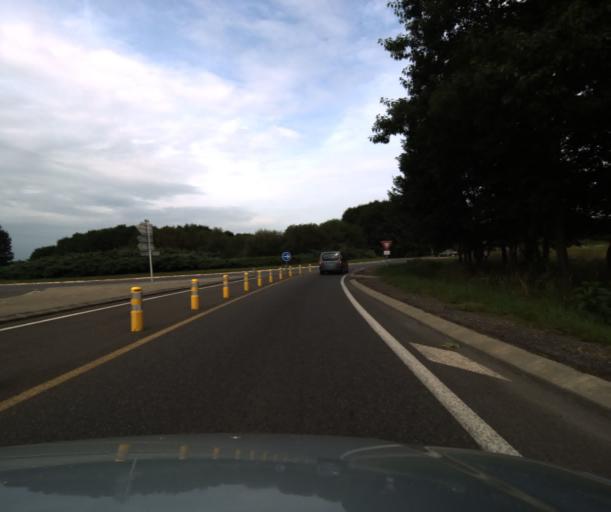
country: FR
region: Midi-Pyrenees
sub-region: Departement des Hautes-Pyrenees
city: Juillan
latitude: 43.2231
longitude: 0.0272
